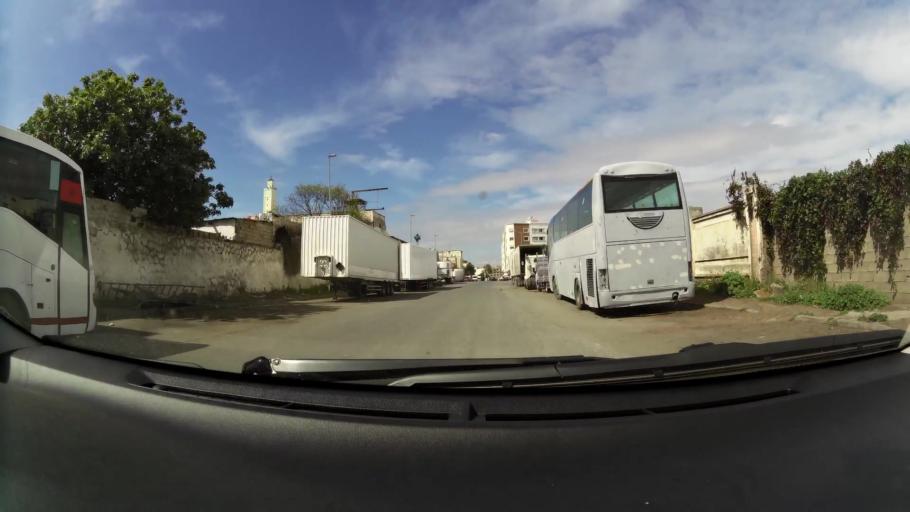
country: MA
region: Grand Casablanca
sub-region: Casablanca
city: Casablanca
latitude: 33.5855
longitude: -7.5914
